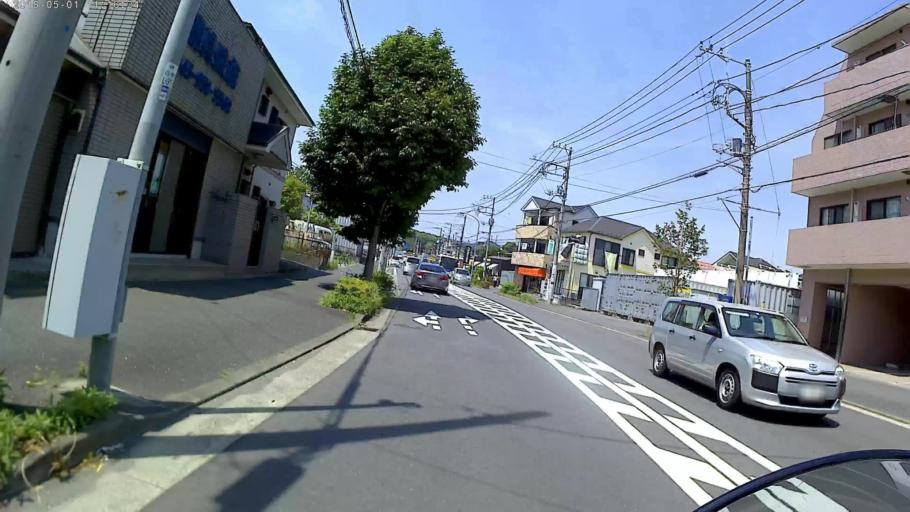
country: JP
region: Kanagawa
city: Minami-rinkan
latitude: 35.4925
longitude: 139.5370
